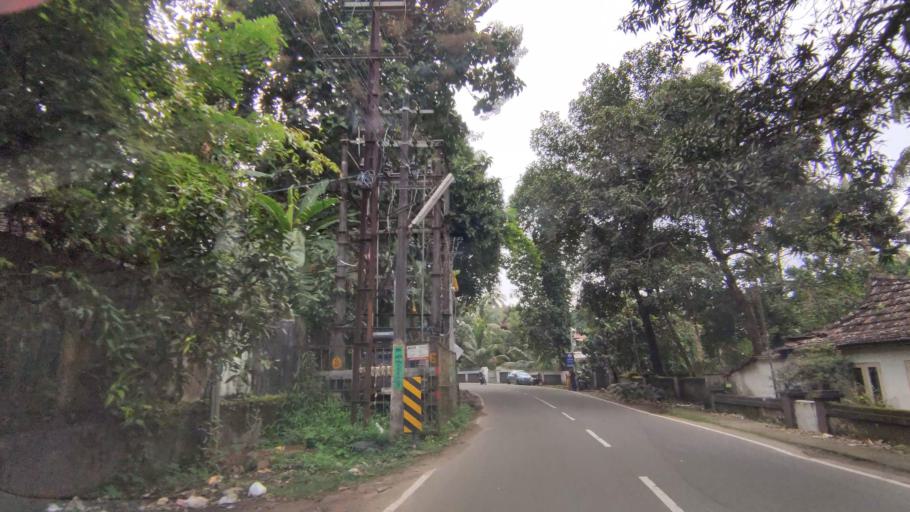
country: IN
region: Kerala
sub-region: Kottayam
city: Kottayam
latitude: 9.5834
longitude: 76.5100
